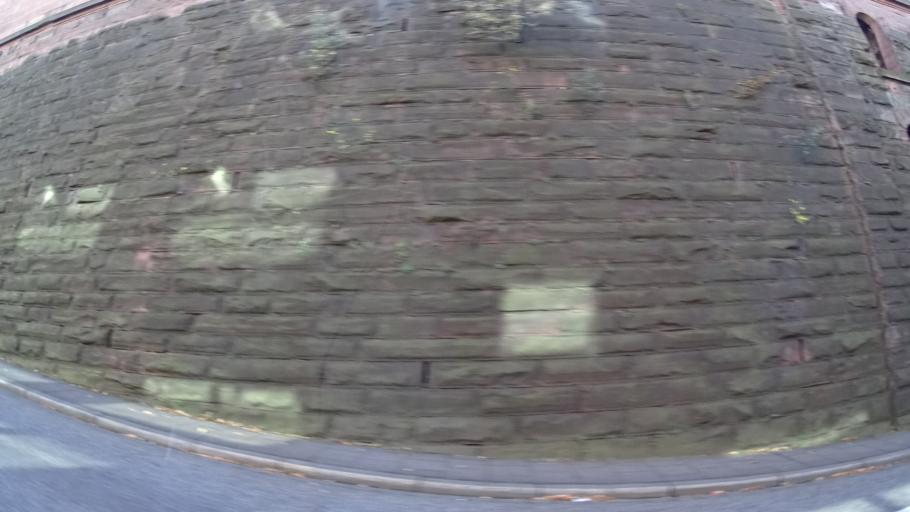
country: DE
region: Baden-Wuerttemberg
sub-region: Karlsruhe Region
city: Pforzheim
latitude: 48.8869
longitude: 8.7061
